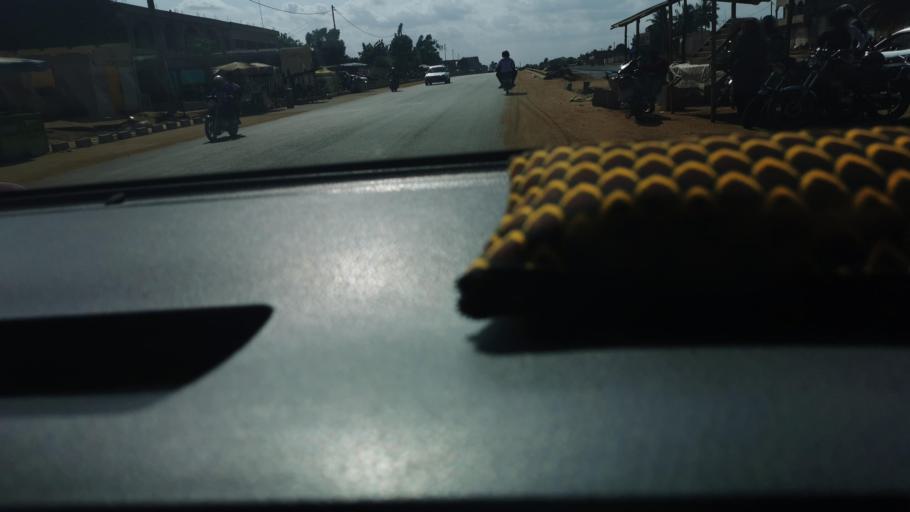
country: TG
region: Maritime
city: Lome
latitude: 6.2171
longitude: 1.1291
